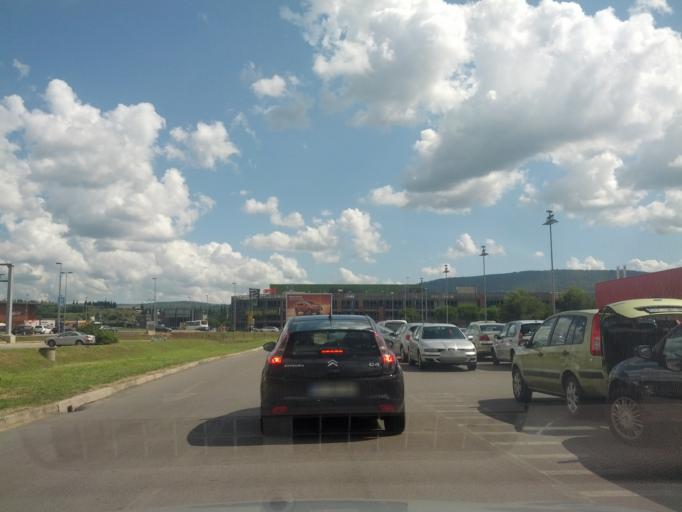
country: SI
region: Koper-Capodistria
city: Koper
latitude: 45.5426
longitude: 13.7342
